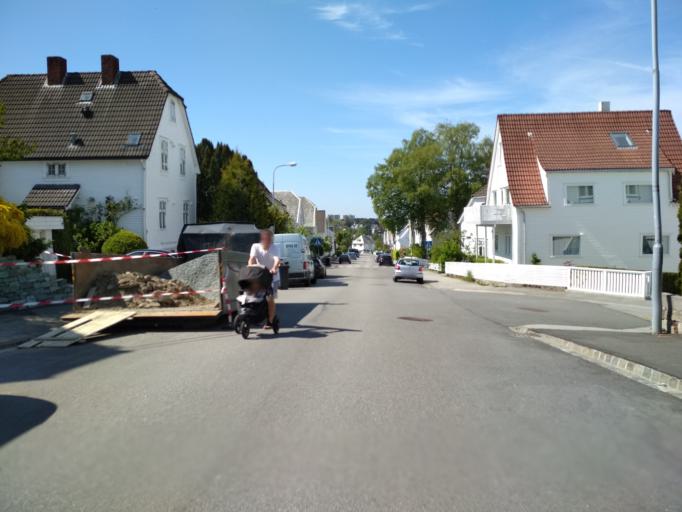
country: NO
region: Rogaland
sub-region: Stavanger
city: Stavanger
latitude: 58.9588
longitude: 5.7297
